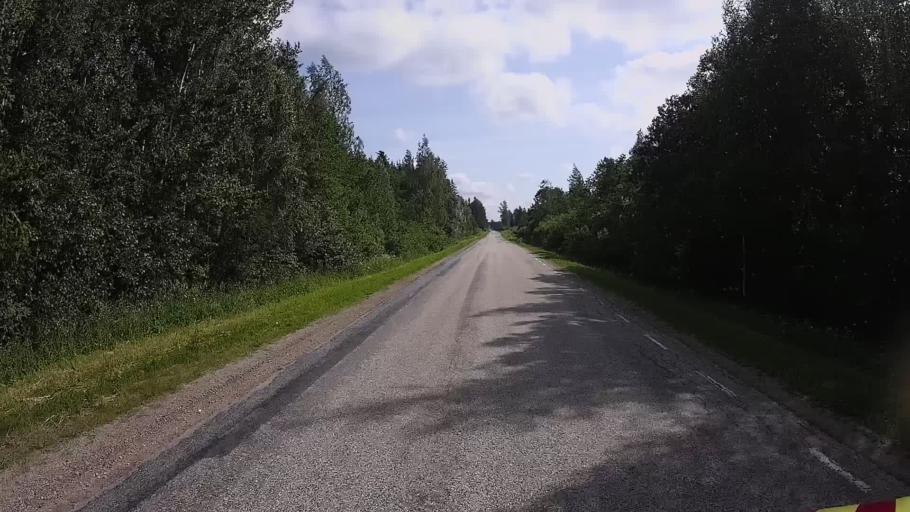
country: EE
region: Vorumaa
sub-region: Antsla vald
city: Vana-Antsla
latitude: 57.8456
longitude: 26.5642
